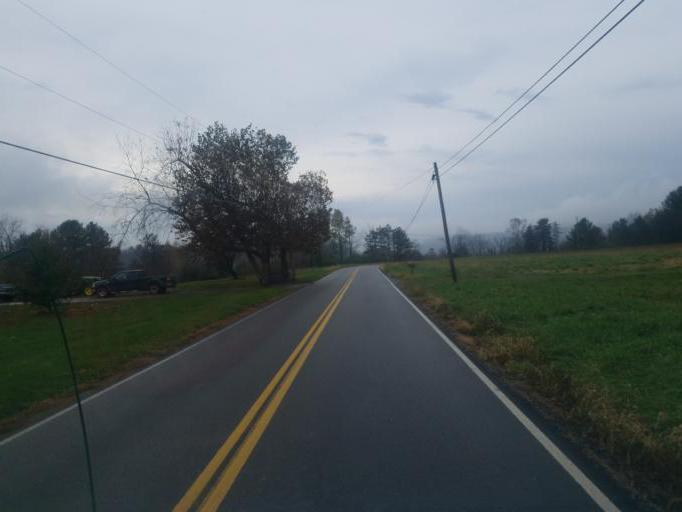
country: US
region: Ohio
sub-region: Morgan County
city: McConnelsville
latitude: 39.5593
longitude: -81.7839
